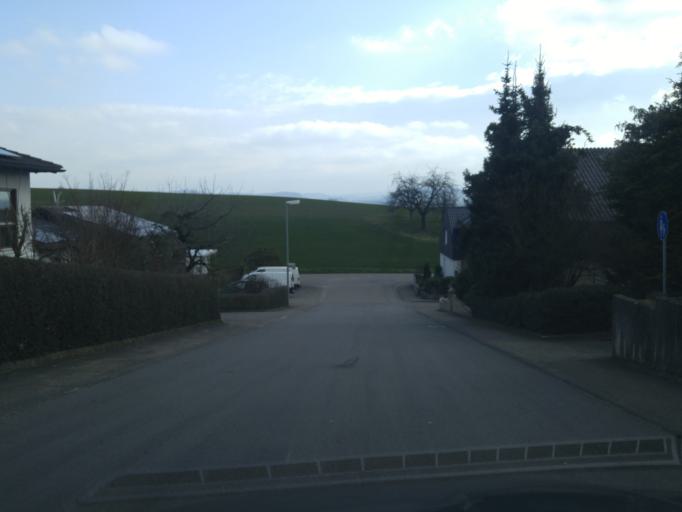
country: DE
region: Baden-Wuerttemberg
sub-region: Regierungsbezirk Stuttgart
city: Ilsfeld
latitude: 49.0604
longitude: 9.2477
